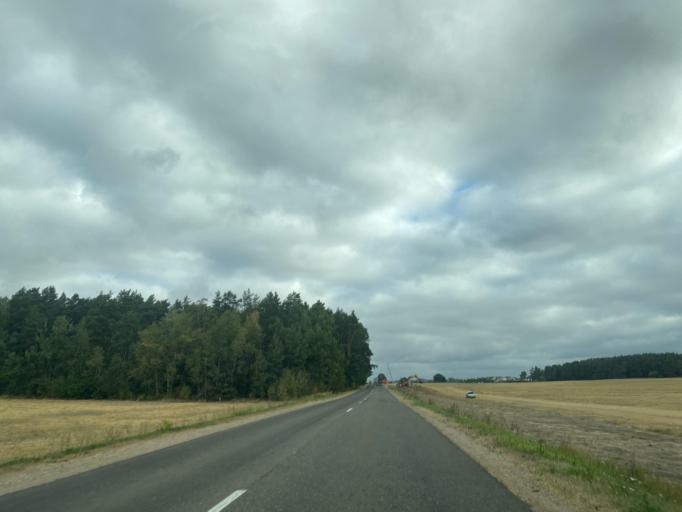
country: BY
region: Minsk
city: Bal'shavik
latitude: 53.9809
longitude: 27.5782
